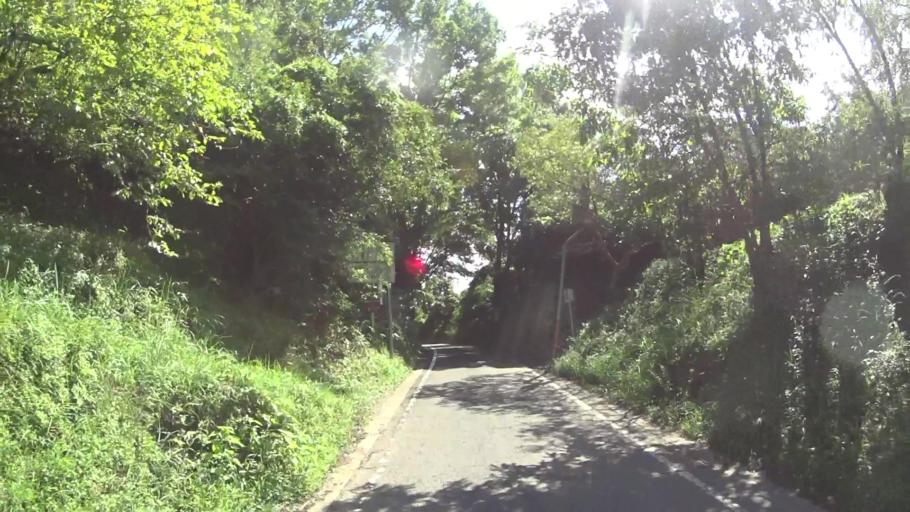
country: JP
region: Nara
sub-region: Ikoma-shi
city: Ikoma
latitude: 34.7503
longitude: 135.7373
